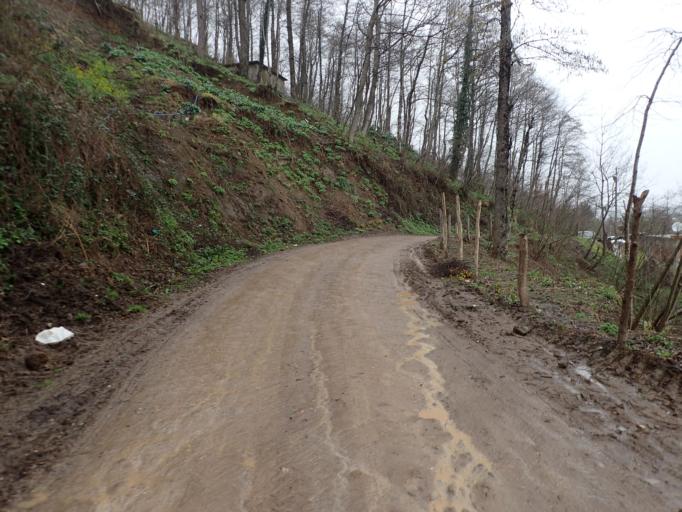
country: TR
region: Ordu
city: Camas
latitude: 40.8817
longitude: 37.4989
